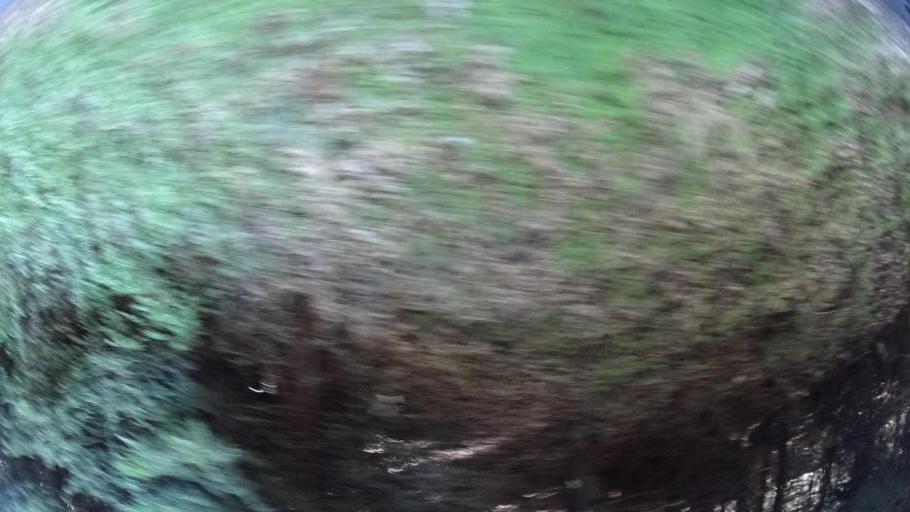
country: US
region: California
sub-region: Humboldt County
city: Rio Dell
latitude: 40.4587
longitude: -124.0022
